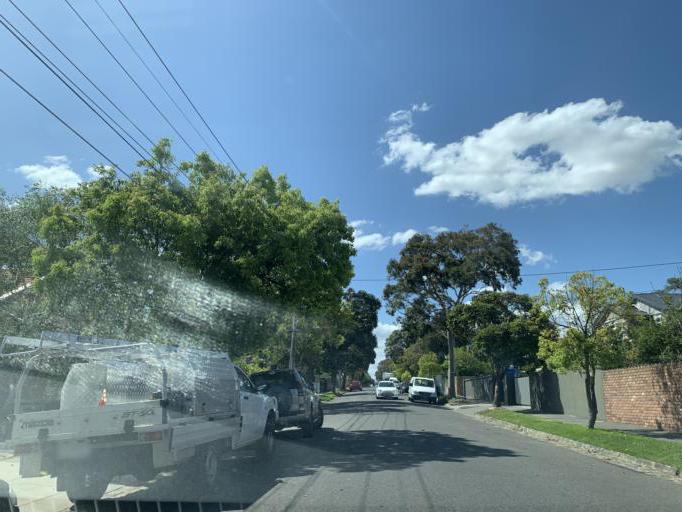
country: AU
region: Victoria
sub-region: Bayside
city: Hampton
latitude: -37.9284
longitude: 145.0017
